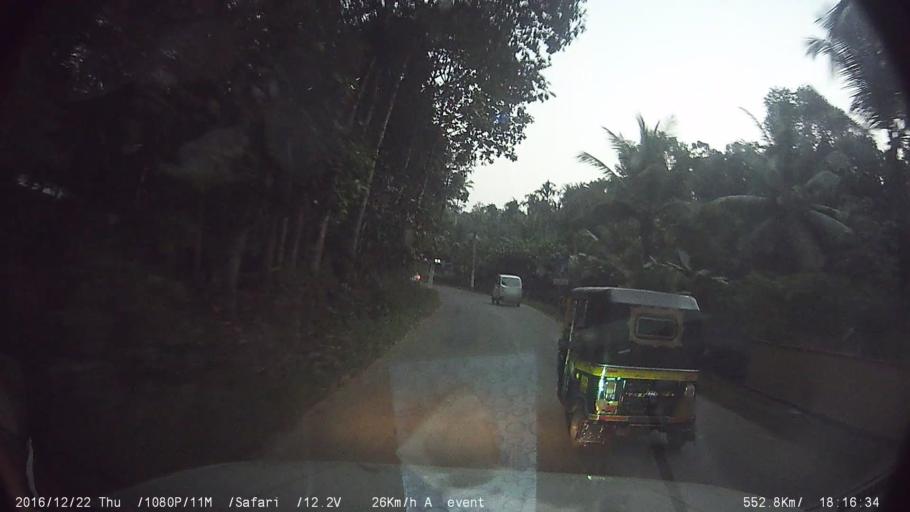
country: IN
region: Kerala
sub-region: Kottayam
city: Palackattumala
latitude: 9.7670
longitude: 76.6104
